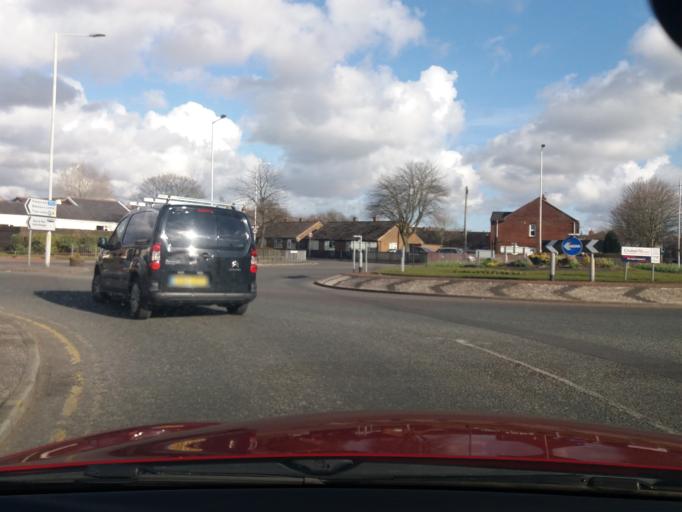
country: GB
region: England
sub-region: Lancashire
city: Chorley
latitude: 53.6479
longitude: -2.6282
